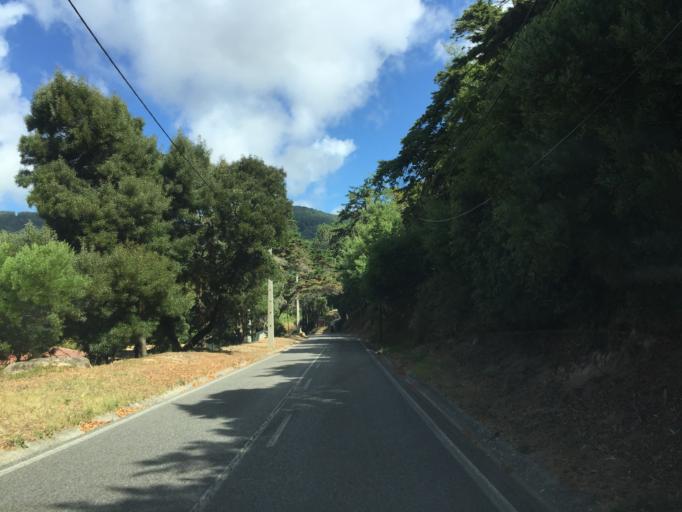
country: PT
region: Lisbon
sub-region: Sintra
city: Colares
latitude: 38.7569
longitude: -9.4449
